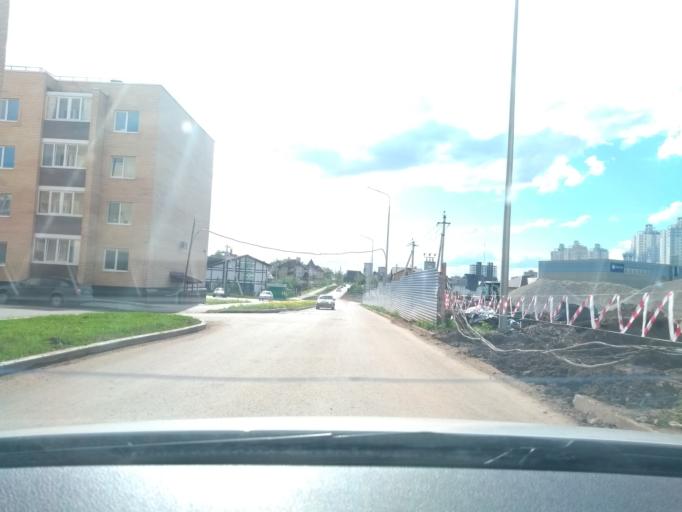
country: RU
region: Perm
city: Perm
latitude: 58.0033
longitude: 56.3352
